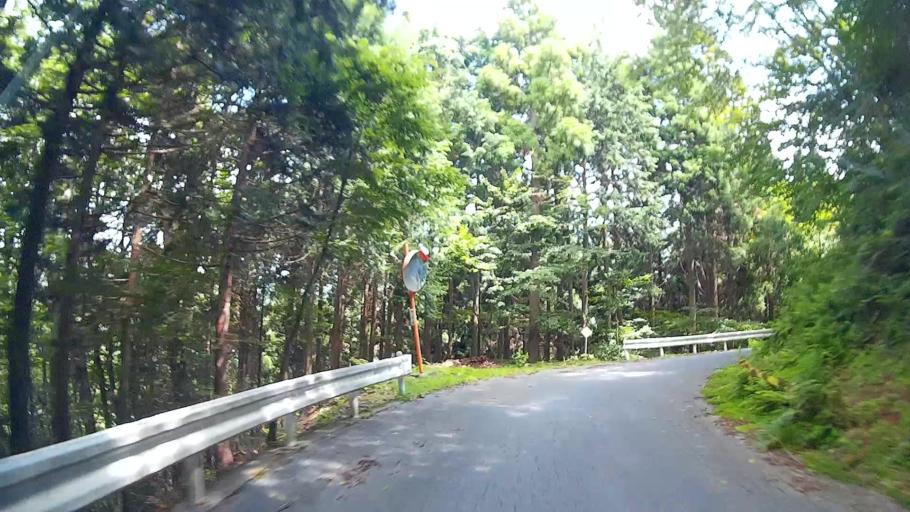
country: JP
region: Saitama
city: Chichibu
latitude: 35.8947
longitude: 139.1083
